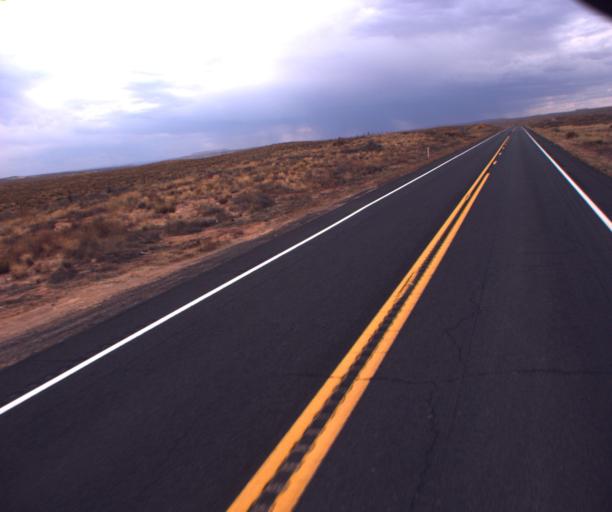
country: US
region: Arizona
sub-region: Coconino County
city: Kaibito
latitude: 36.3973
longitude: -110.8642
